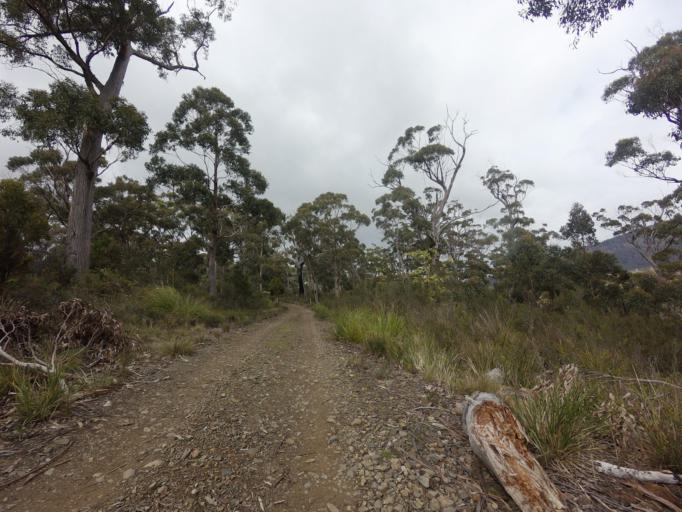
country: AU
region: Tasmania
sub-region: Huon Valley
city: Geeveston
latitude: -43.4596
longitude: 146.9095
